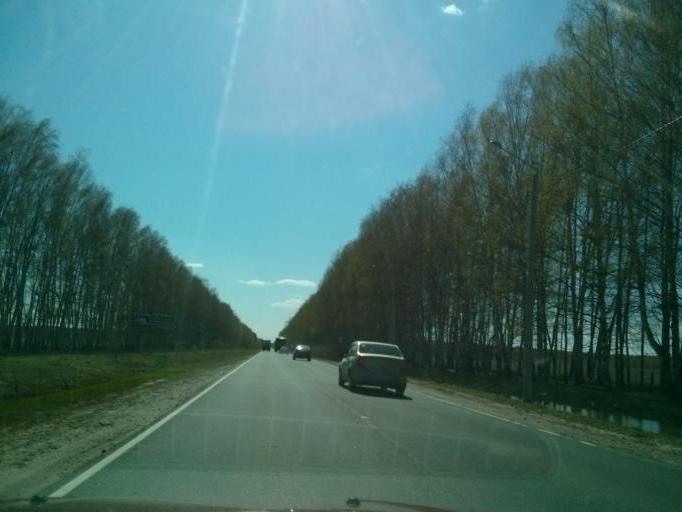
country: RU
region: Nizjnij Novgorod
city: Vorsma
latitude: 56.0321
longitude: 43.3638
